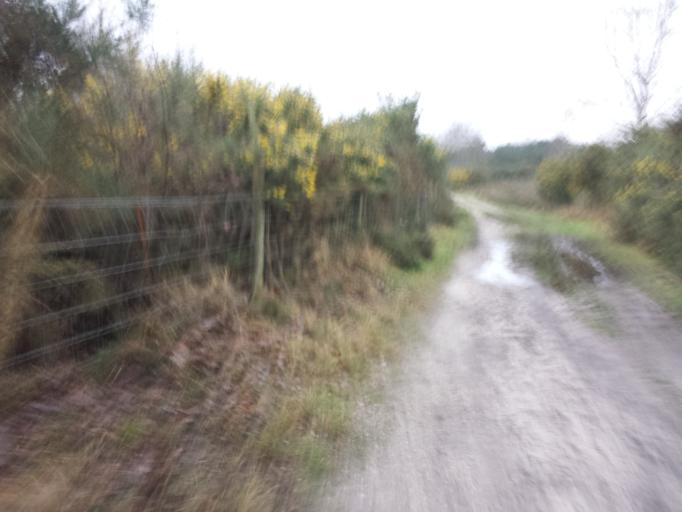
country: GB
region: England
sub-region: Surrey
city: Bagshot
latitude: 51.3511
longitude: -0.6889
